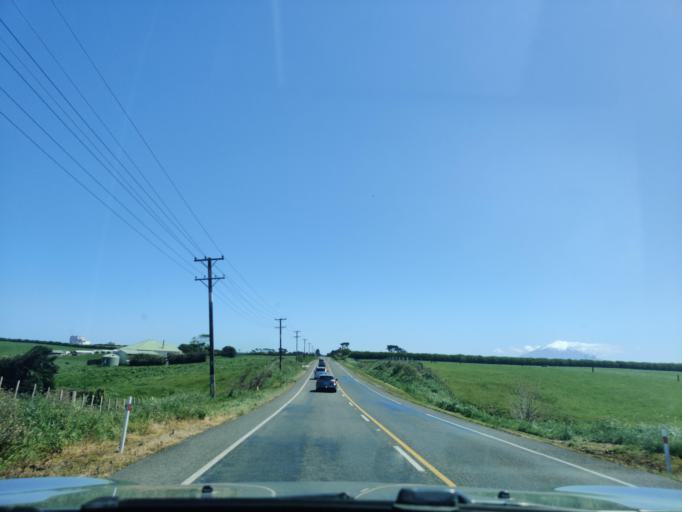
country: NZ
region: Taranaki
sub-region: South Taranaki District
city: Hawera
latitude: -39.6121
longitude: 174.3284
